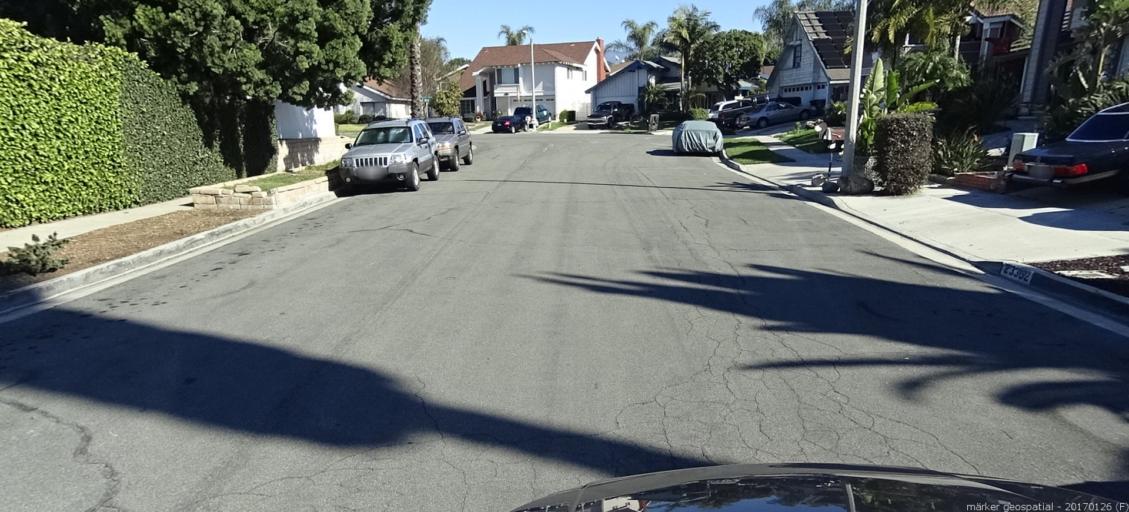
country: US
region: California
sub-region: Orange County
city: Lake Forest
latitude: 33.6238
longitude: -117.6851
